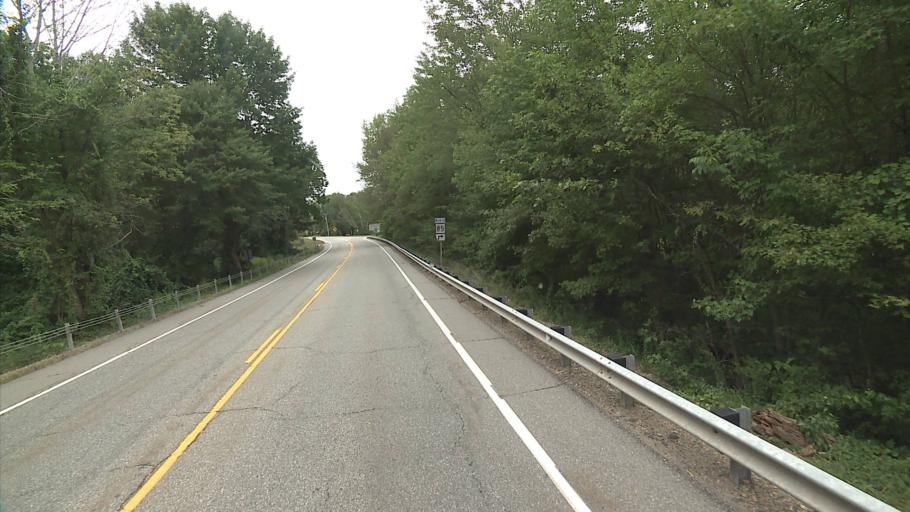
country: US
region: Connecticut
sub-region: Hartford County
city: Terramuggus
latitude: 41.6919
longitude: -72.4364
